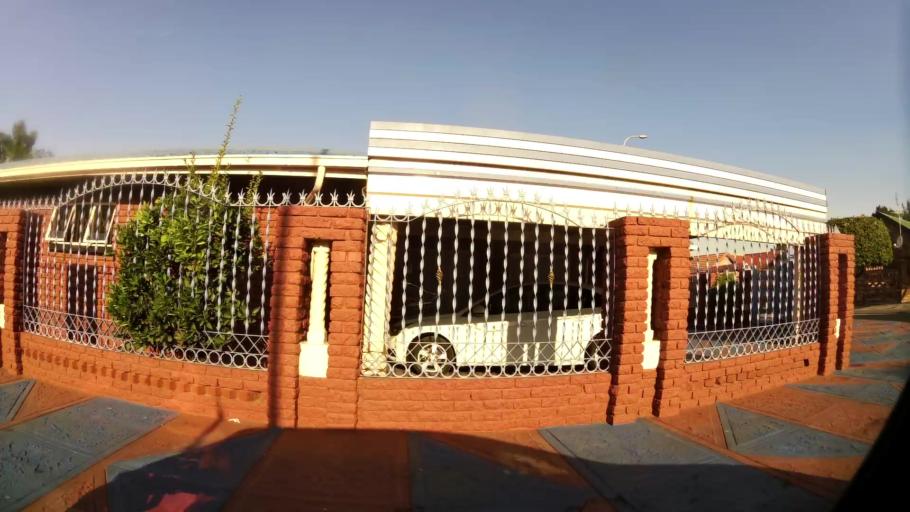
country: ZA
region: North-West
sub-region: Bojanala Platinum District Municipality
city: Rustenburg
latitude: -25.6509
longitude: 27.2181
